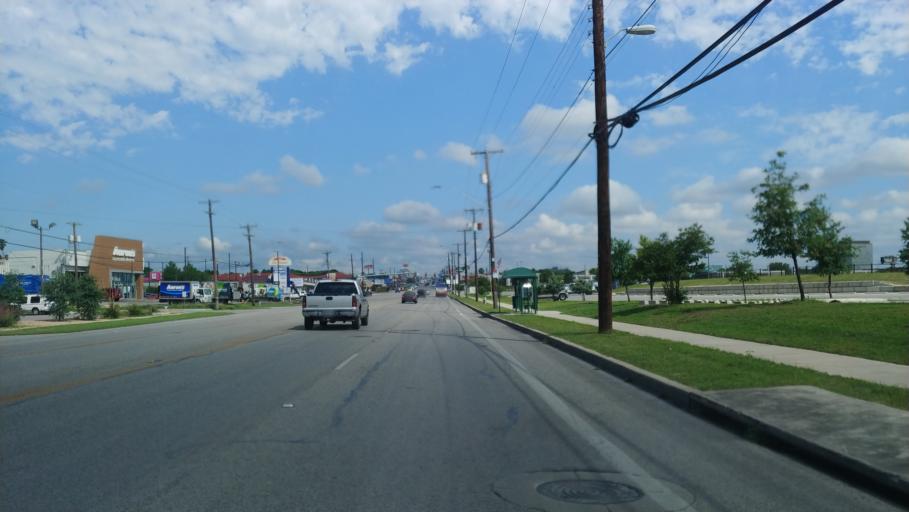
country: US
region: Texas
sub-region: Bexar County
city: Balcones Heights
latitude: 29.4782
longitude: -98.5396
